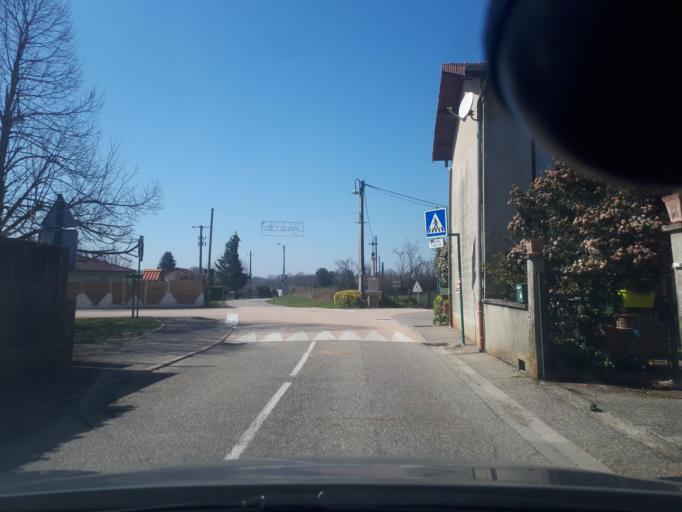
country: FR
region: Rhone-Alpes
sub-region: Departement de l'Isere
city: Nivolas-Vermelle
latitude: 45.5287
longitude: 5.3380
